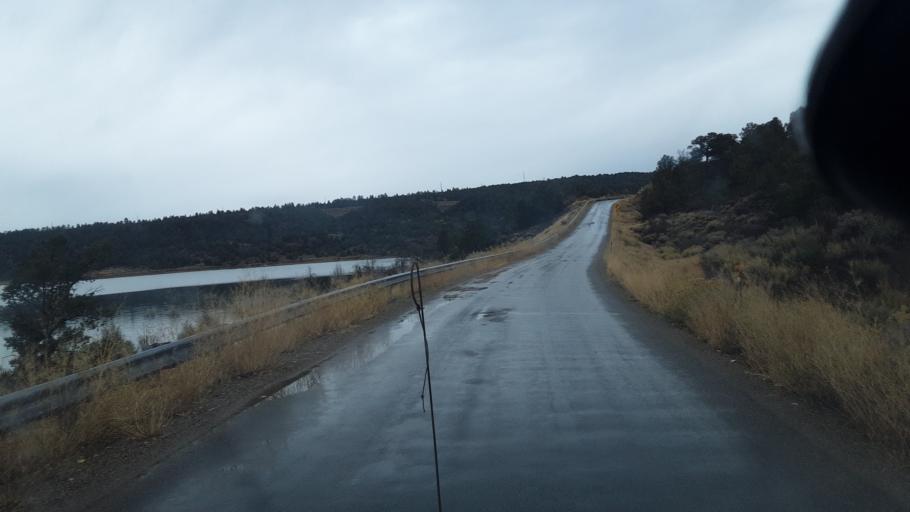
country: US
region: Colorado
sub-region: La Plata County
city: Durango
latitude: 37.2341
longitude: -107.9066
